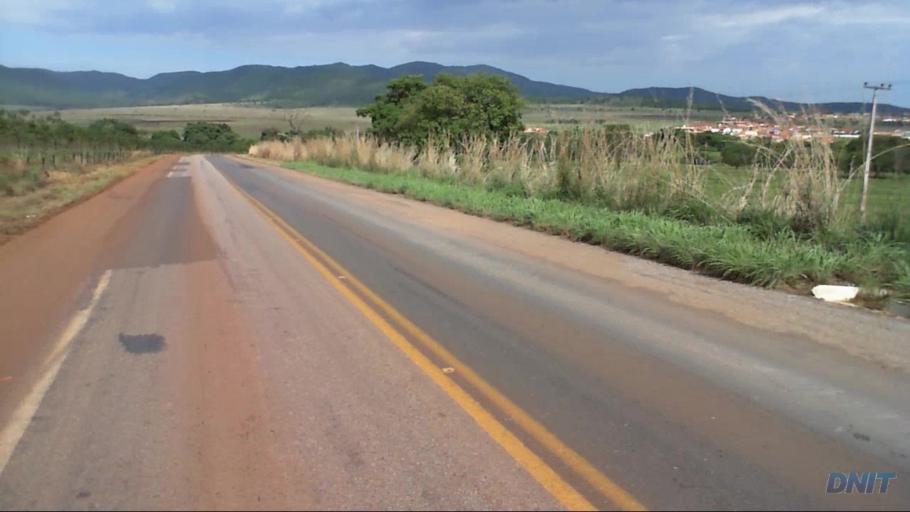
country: BR
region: Goias
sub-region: Barro Alto
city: Barro Alto
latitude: -14.9872
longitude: -48.9180
